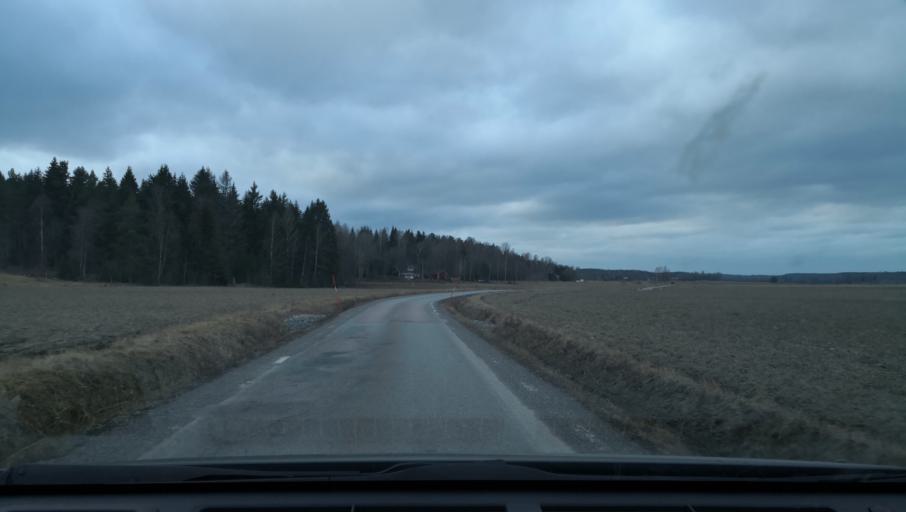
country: SE
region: Vaestmanland
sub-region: Kopings Kommun
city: Kolsva
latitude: 59.5506
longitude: 15.8775
